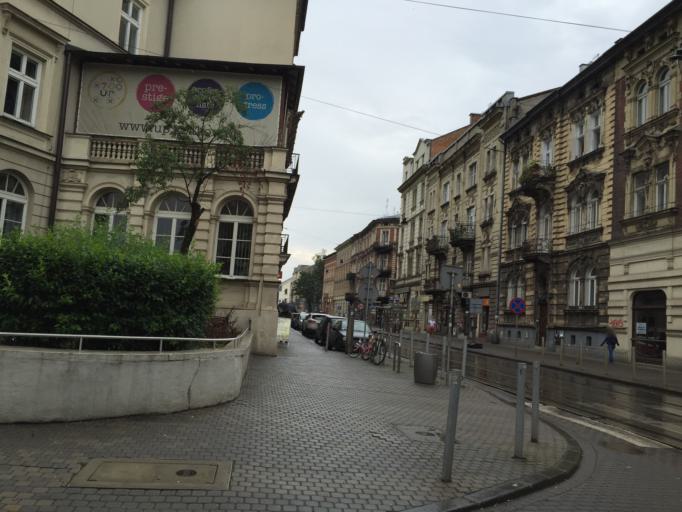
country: PL
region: Lesser Poland Voivodeship
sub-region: Krakow
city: Krakow
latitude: 50.0675
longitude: 19.9285
